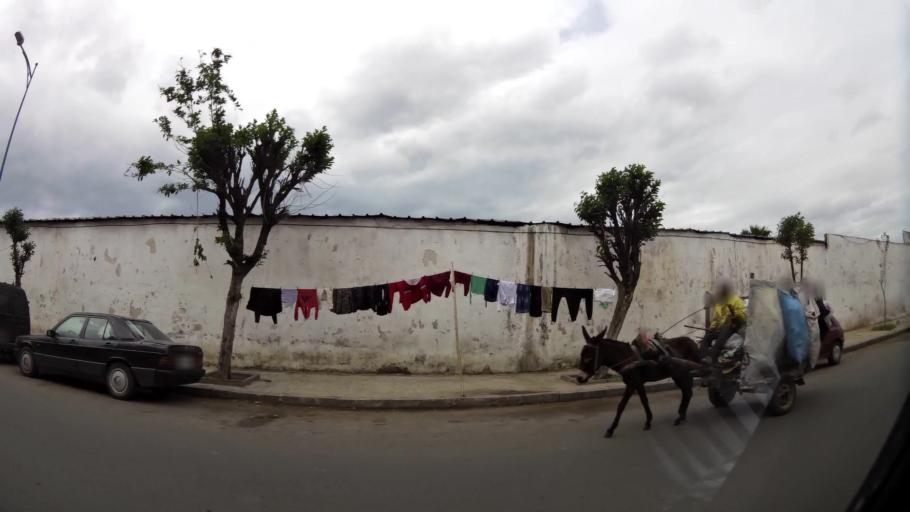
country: MA
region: Grand Casablanca
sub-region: Casablanca
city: Casablanca
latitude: 33.5957
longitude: -7.5670
